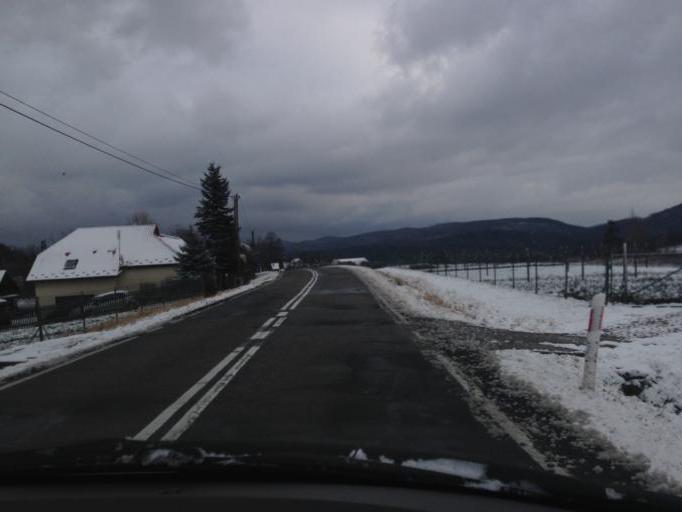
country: PL
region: Lesser Poland Voivodeship
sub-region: Powiat bochenski
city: Nowy Wisnicz
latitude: 49.8507
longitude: 20.4888
